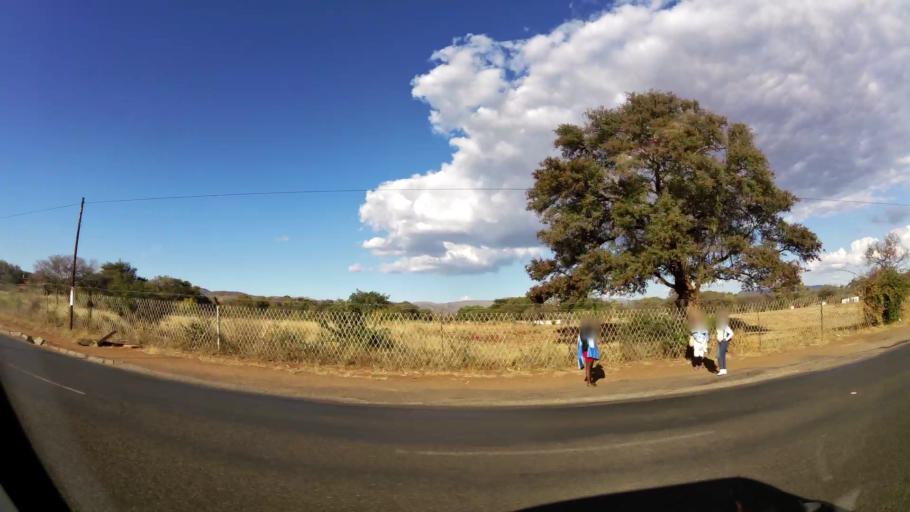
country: ZA
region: Limpopo
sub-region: Waterberg District Municipality
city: Mokopane
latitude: -24.1968
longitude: 29.0081
